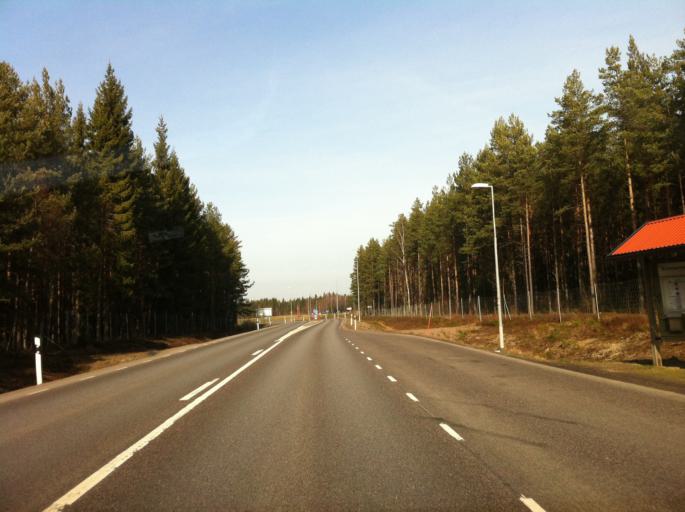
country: SE
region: Vaestra Goetaland
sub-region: Tidaholms Kommun
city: Tidaholm
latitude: 58.1363
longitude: 13.8959
